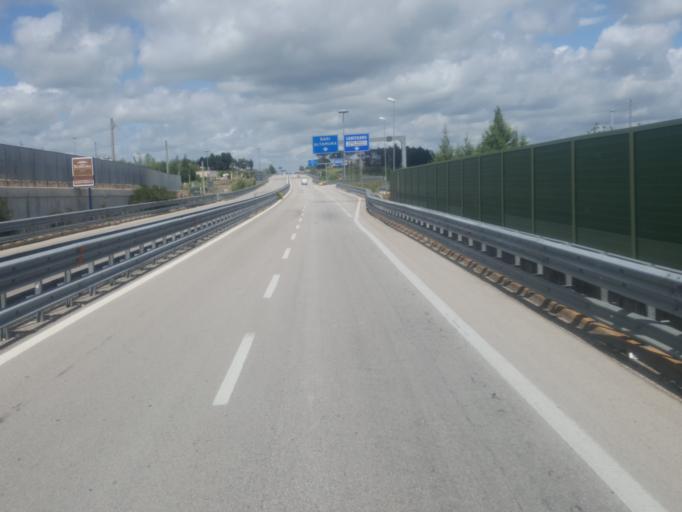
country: IT
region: Basilicate
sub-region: Provincia di Matera
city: Matera
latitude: 40.6961
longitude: 16.5909
